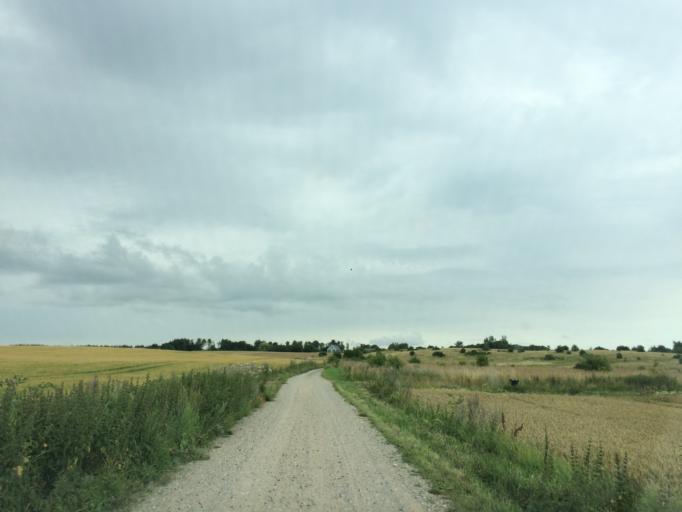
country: DK
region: Central Jutland
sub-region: Syddjurs Kommune
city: Ronde
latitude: 56.2357
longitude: 10.5501
